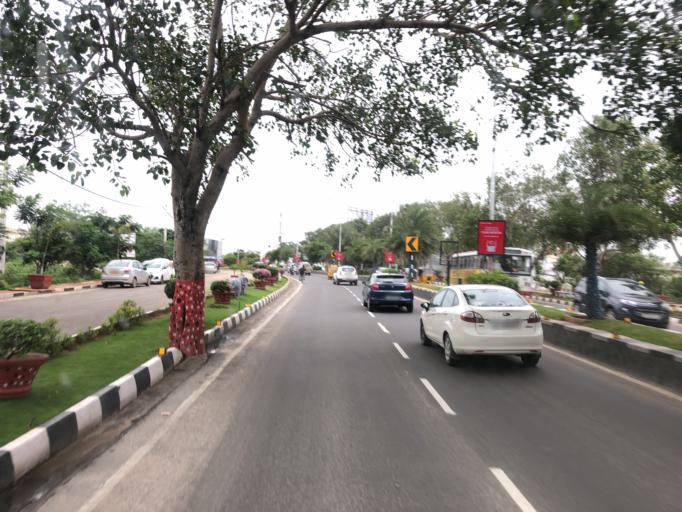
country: IN
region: Telangana
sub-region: Rangareddi
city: Kukatpalli
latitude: 17.4621
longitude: 78.3765
